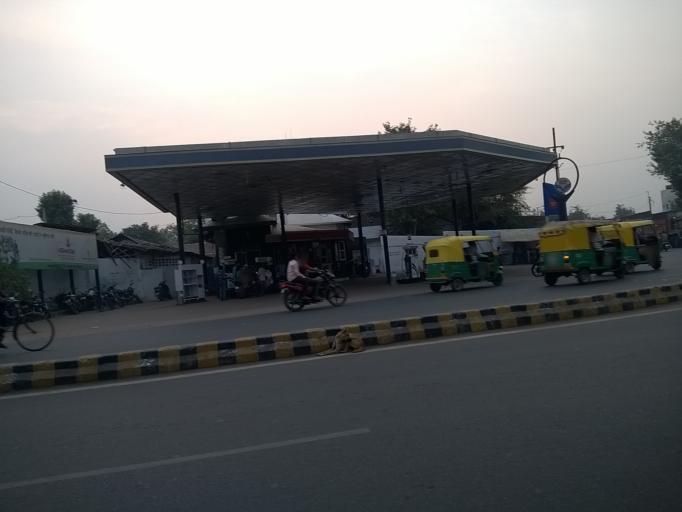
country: IN
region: Gujarat
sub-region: Kheda
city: Nadiad
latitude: 22.6988
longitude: 72.8566
